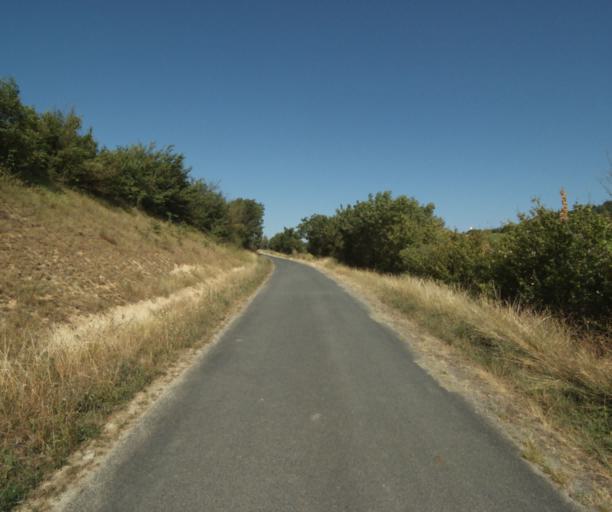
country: FR
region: Midi-Pyrenees
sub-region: Departement de la Haute-Garonne
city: Saint-Felix-Lauragais
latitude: 43.5074
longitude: 1.9344
